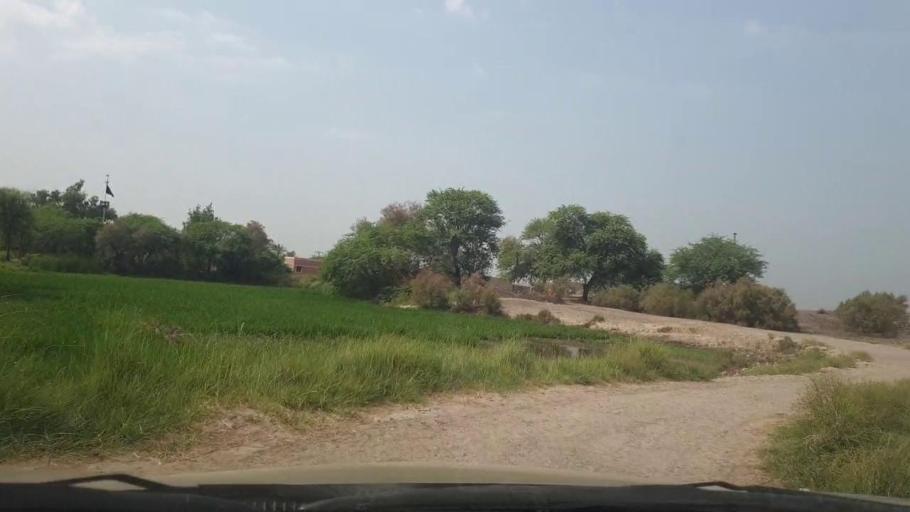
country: PK
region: Sindh
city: Larkana
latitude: 27.6810
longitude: 68.2026
